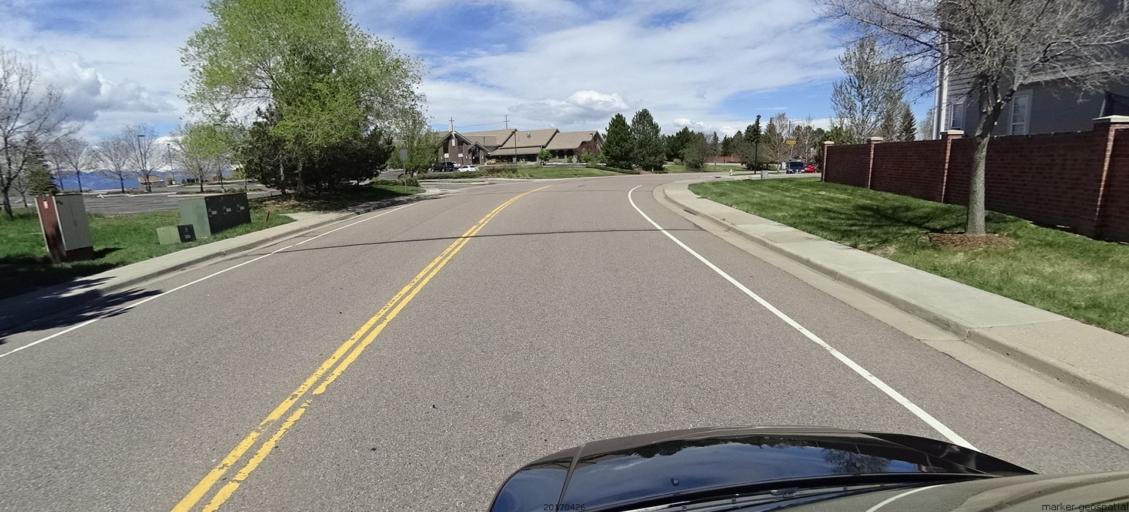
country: US
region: Colorado
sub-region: Douglas County
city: Carriage Club
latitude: 39.5350
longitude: -104.9016
